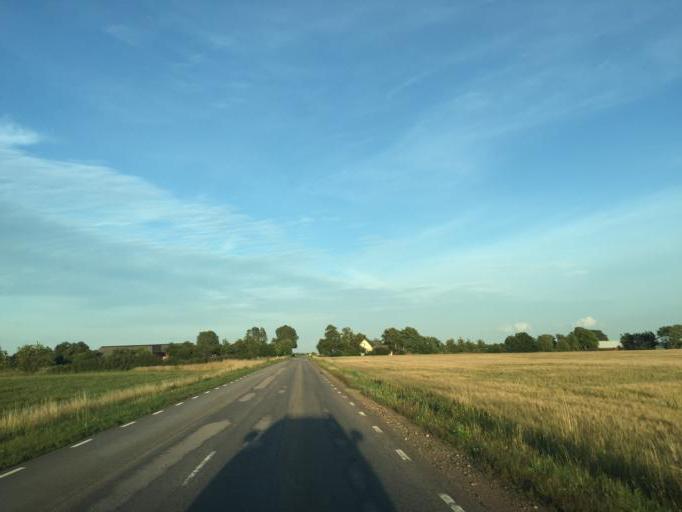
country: SE
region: Skane
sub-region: Angelholms Kommun
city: Vejbystrand
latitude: 56.3132
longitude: 12.8020
